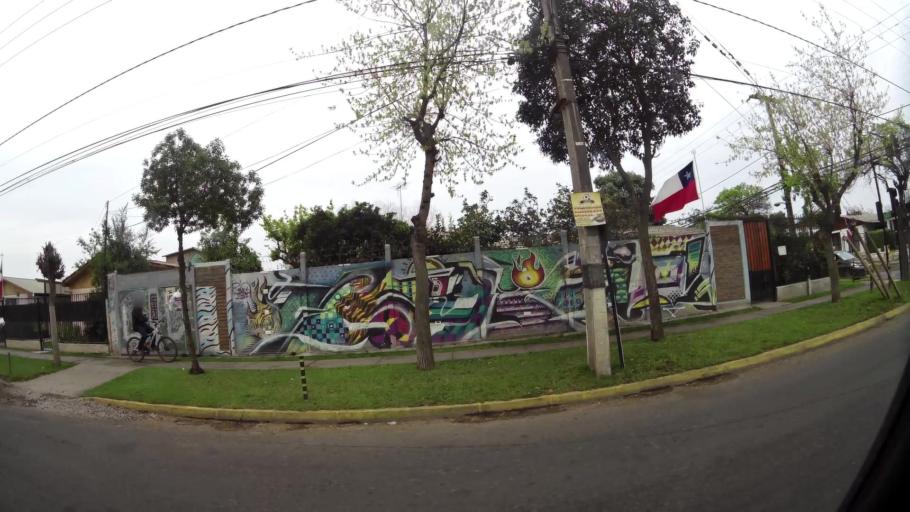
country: CL
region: Santiago Metropolitan
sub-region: Provincia de Santiago
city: Lo Prado
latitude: -33.5177
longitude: -70.7688
